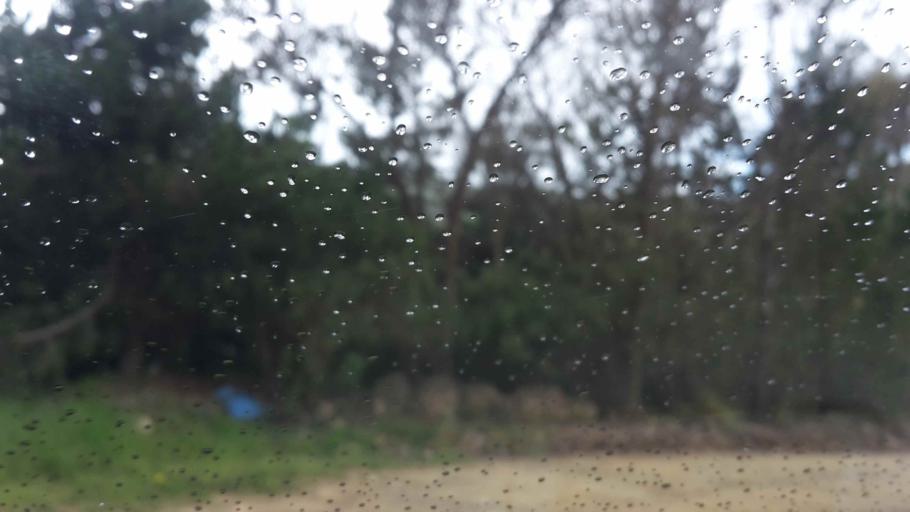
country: BO
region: Cochabamba
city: Cochabamba
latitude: -17.1359
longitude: -66.1053
